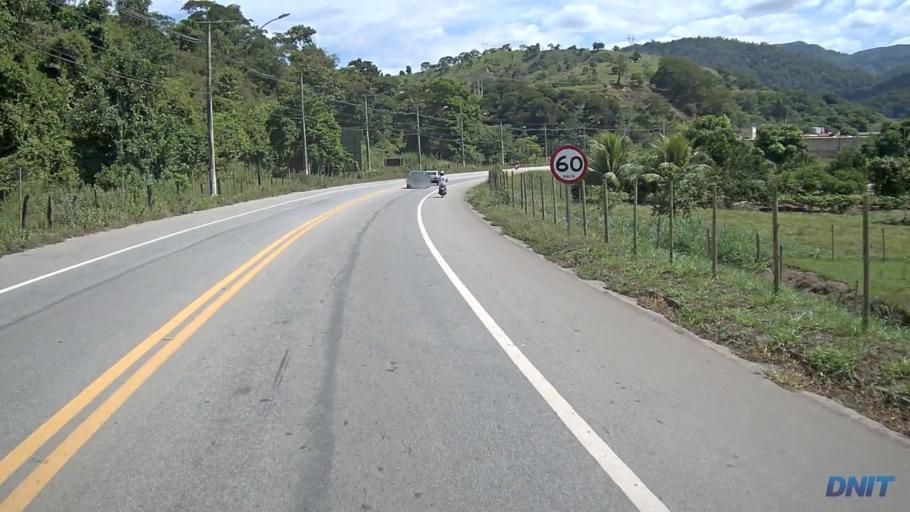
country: BR
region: Minas Gerais
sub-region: Timoteo
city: Timoteo
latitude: -19.5448
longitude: -42.6780
